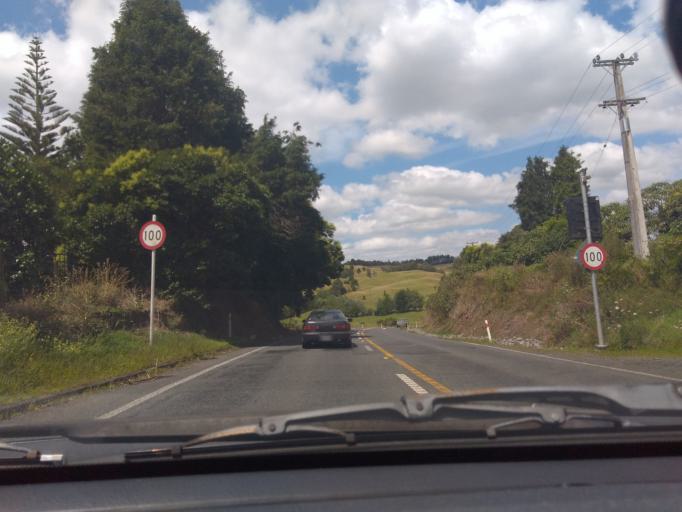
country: NZ
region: Northland
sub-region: Far North District
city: Moerewa
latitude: -35.3568
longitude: 173.9580
